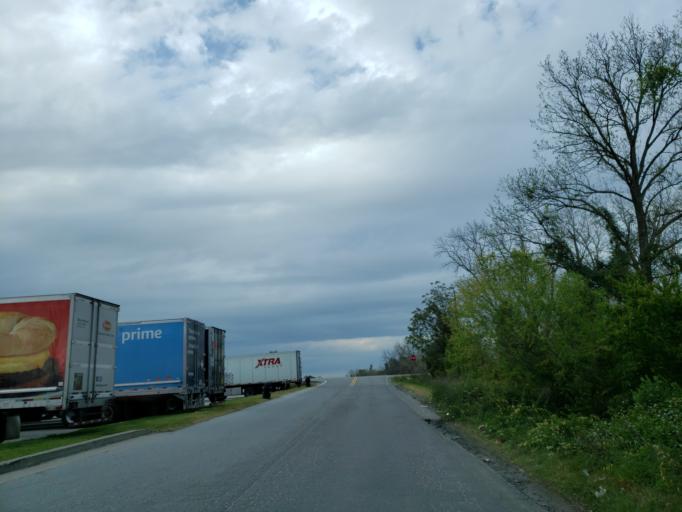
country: US
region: Georgia
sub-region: Dooly County
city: Vienna
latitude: 32.0850
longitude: -83.7590
